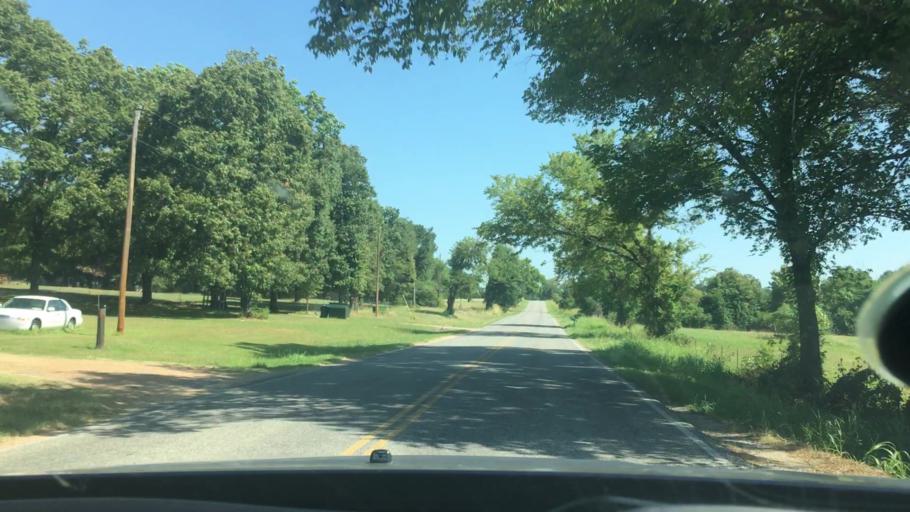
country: US
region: Oklahoma
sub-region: Johnston County
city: Tishomingo
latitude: 34.2509
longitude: -96.6186
